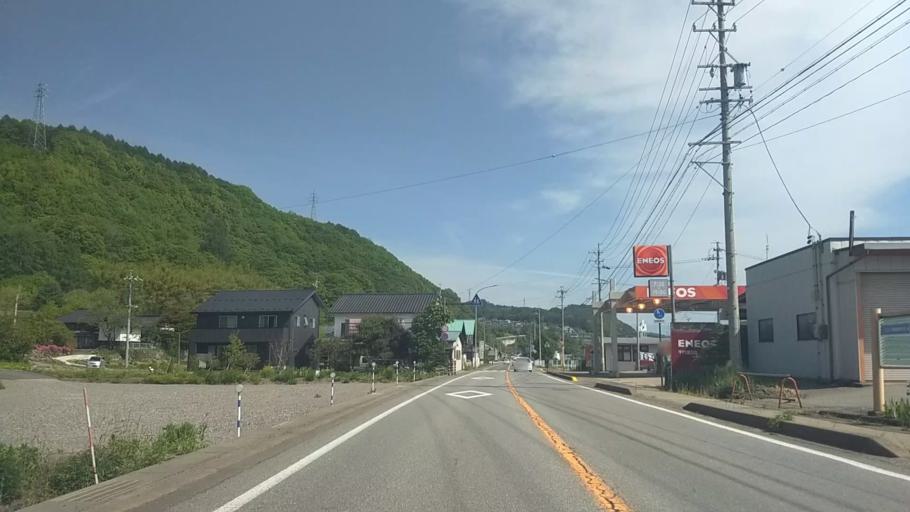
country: JP
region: Nagano
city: Saku
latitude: 36.1205
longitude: 138.4703
